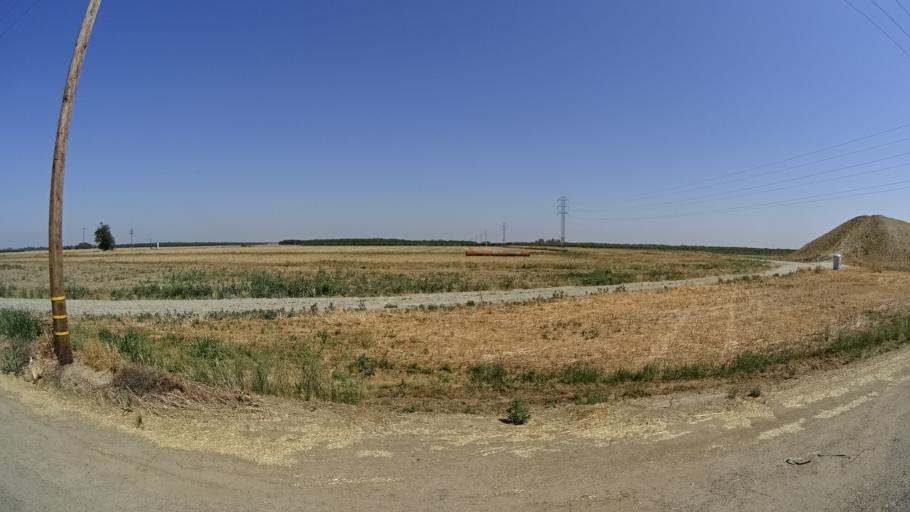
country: US
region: California
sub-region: Kings County
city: Hanford
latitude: 36.3714
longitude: -119.5924
